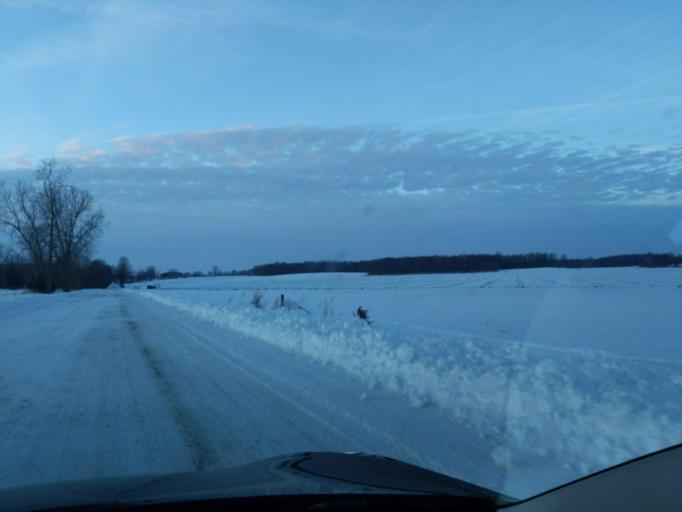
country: US
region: Michigan
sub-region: Ingham County
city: Williamston
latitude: 42.5616
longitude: -84.3054
